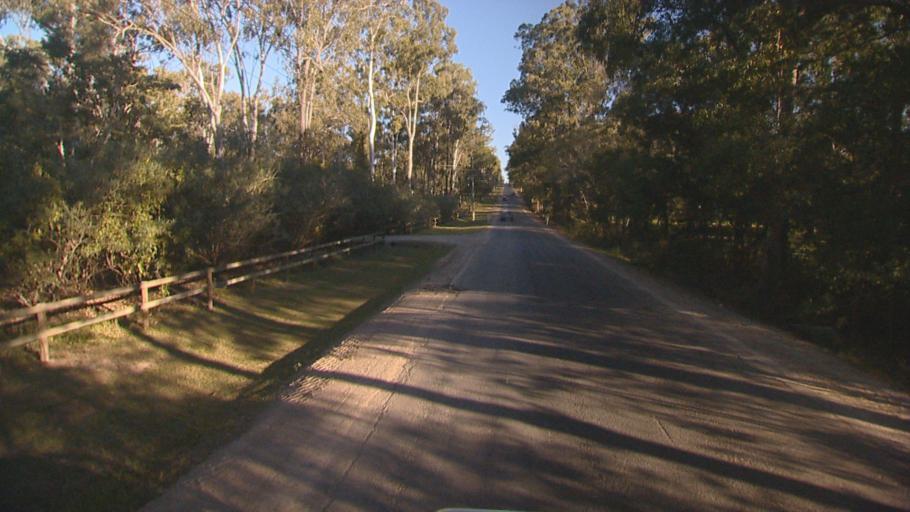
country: AU
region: Queensland
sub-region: Logan
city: Chambers Flat
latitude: -27.7721
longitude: 153.1372
